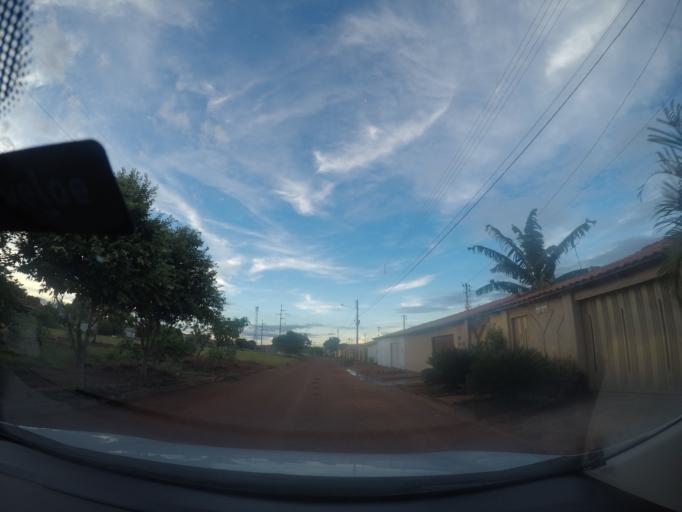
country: BR
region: Goias
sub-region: Goianira
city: Goianira
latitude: -16.5758
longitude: -49.3805
